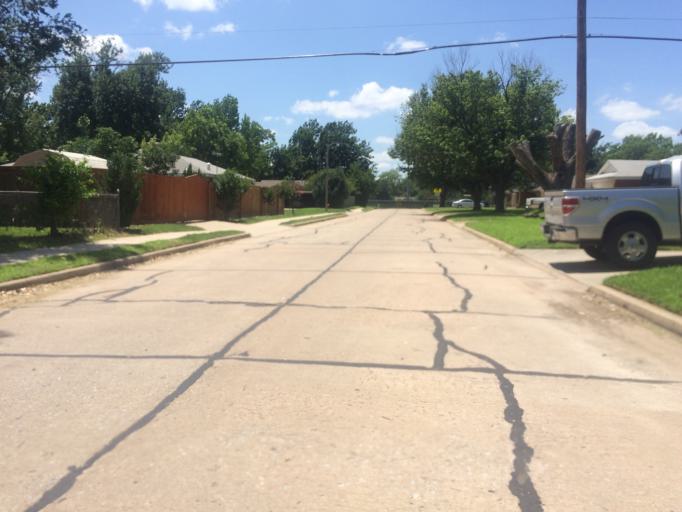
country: US
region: Oklahoma
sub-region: Cleveland County
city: Norman
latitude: 35.2144
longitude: -97.4676
